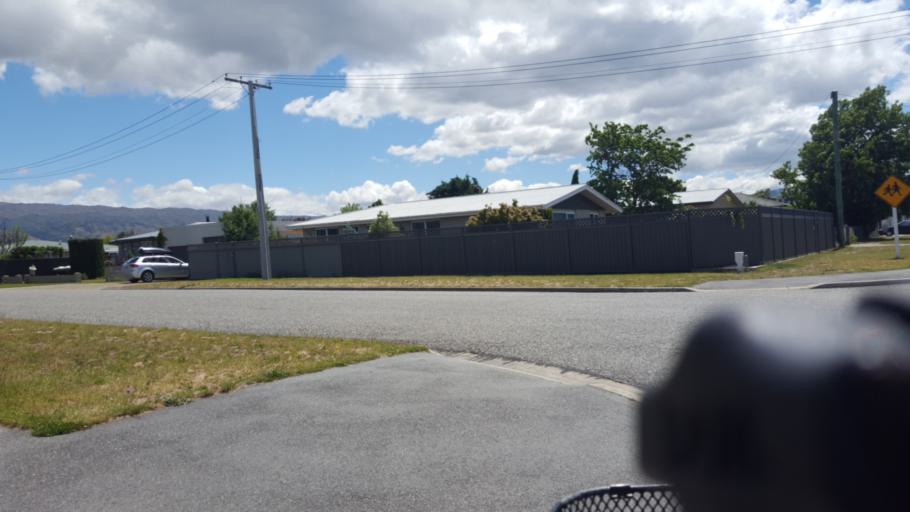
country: NZ
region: Otago
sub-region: Queenstown-Lakes District
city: Wanaka
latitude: -45.2455
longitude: 169.3912
